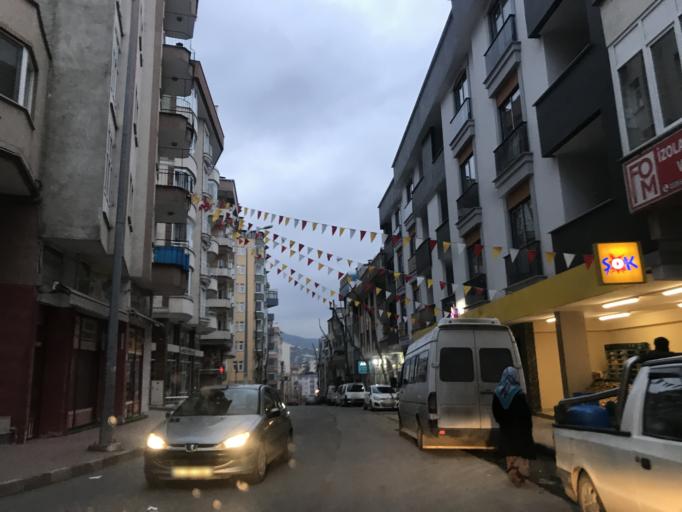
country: TR
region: Trabzon
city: Akcaabat
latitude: 41.0183
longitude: 39.5824
